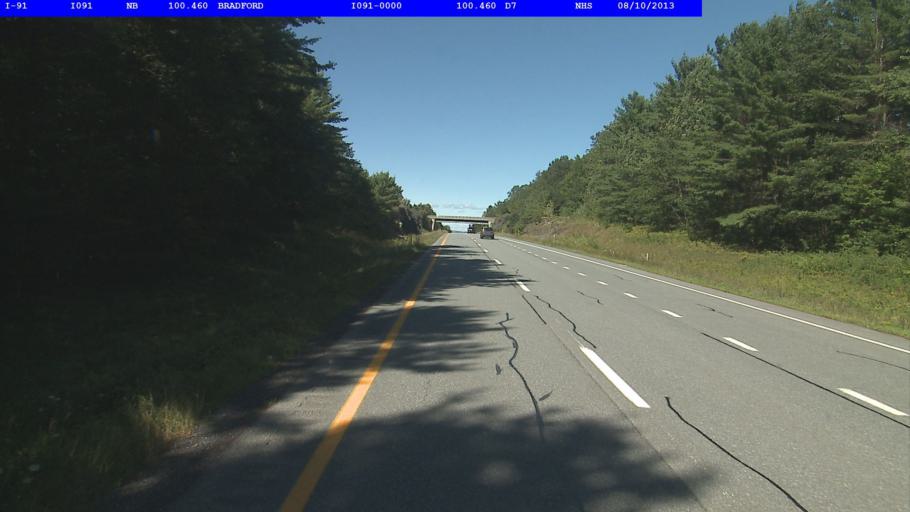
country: US
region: New Hampshire
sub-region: Grafton County
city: Haverhill
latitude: 44.0213
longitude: -72.1178
